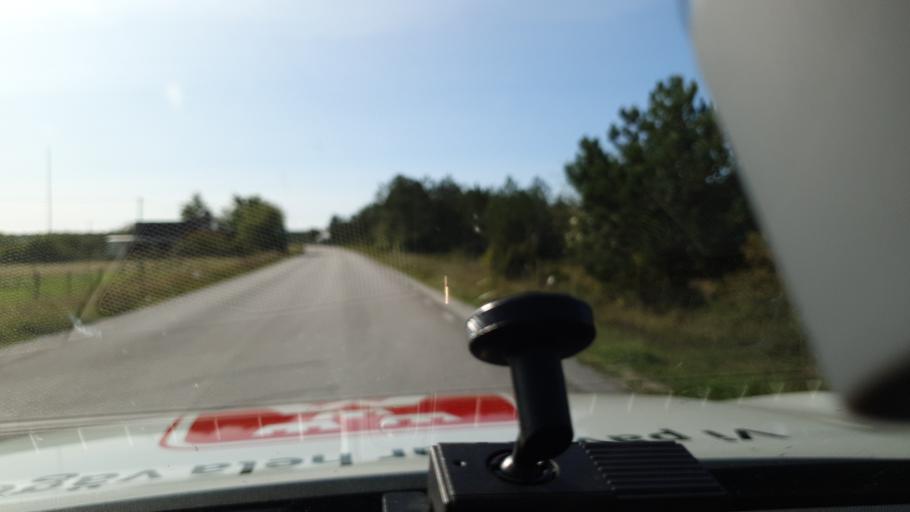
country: SE
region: Gotland
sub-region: Gotland
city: Hemse
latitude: 57.1203
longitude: 18.2753
